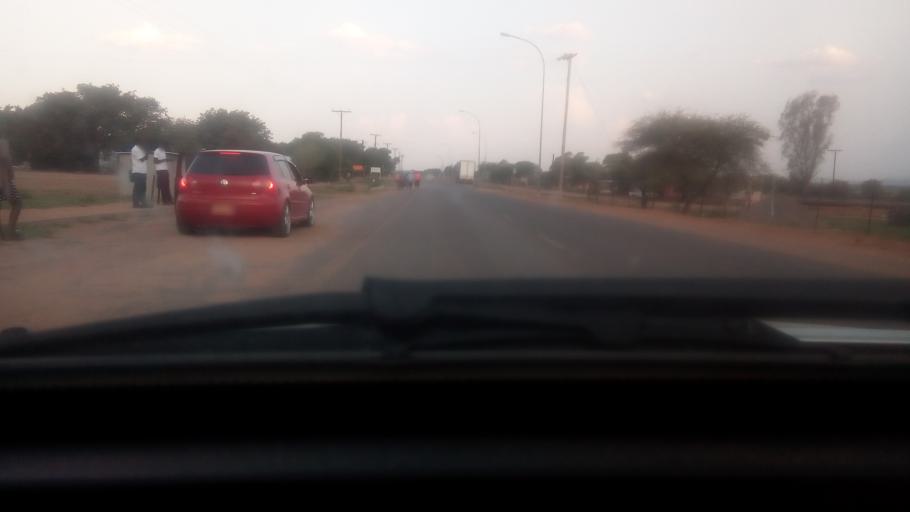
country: BW
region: Kgatleng
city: Bokaa
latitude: -24.4303
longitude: 26.0244
